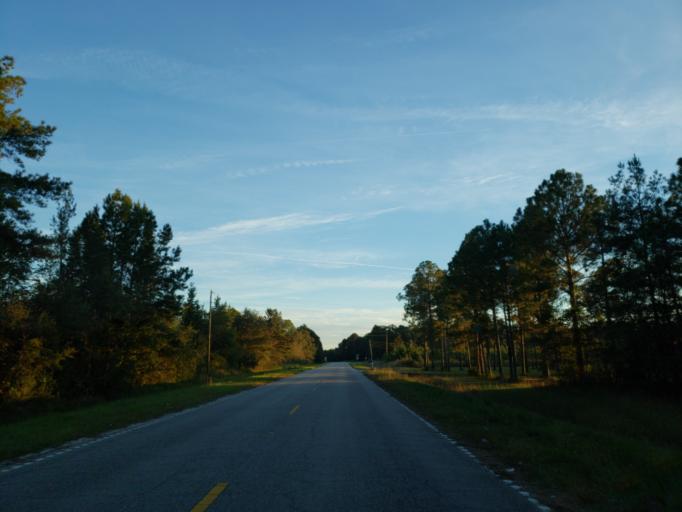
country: US
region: Mississippi
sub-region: Wayne County
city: Belmont
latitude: 31.4180
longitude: -88.4710
